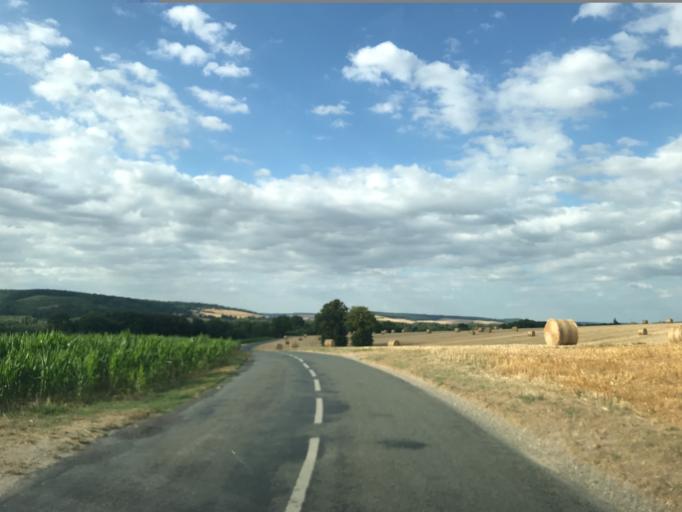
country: FR
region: Ile-de-France
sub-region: Departement des Yvelines
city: Freneuse
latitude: 49.0695
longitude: 1.5908
